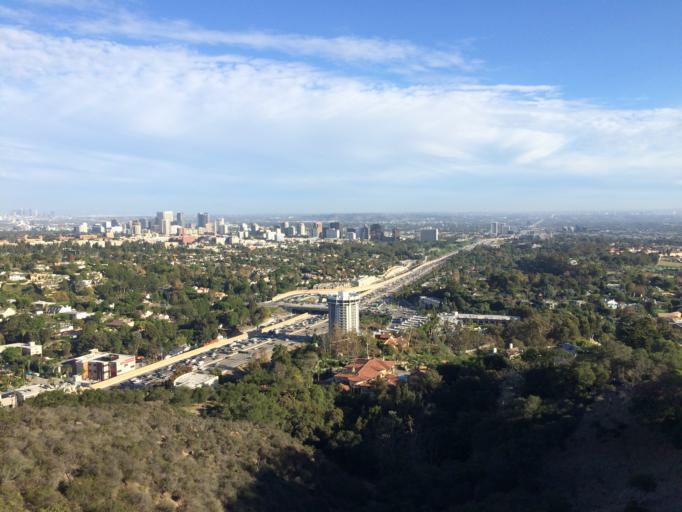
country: US
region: California
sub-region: Los Angeles County
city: Westwood, Los Angeles
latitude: 34.0767
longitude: -118.4731
